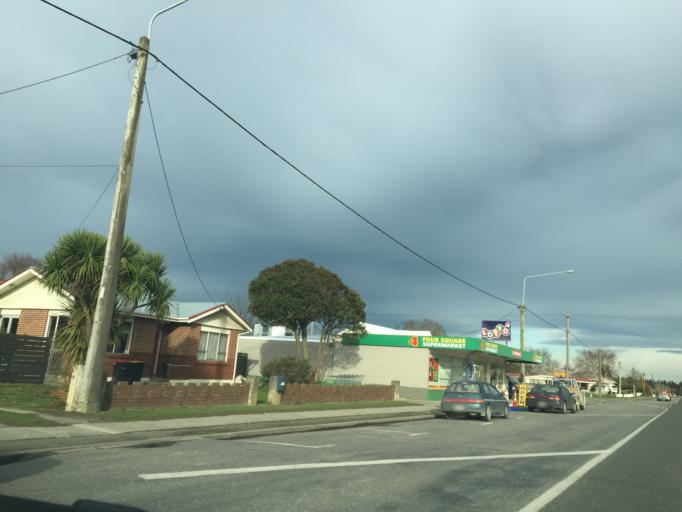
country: NZ
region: Southland
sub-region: Gore District
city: Gore
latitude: -46.1966
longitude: 168.8610
